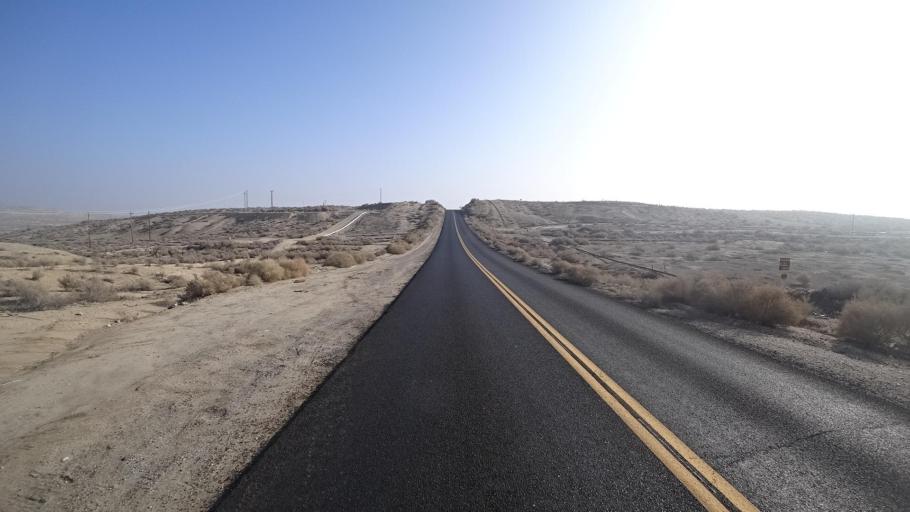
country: US
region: California
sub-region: Kern County
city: Ford City
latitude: 35.1806
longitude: -119.4705
